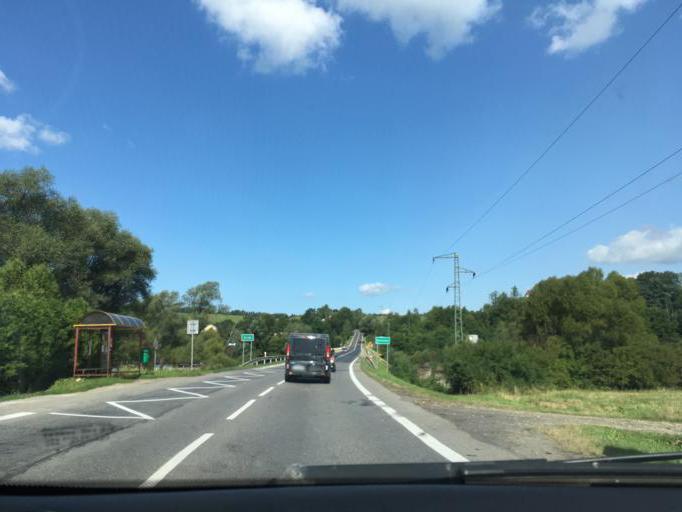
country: PL
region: Subcarpathian Voivodeship
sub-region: Powiat leski
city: Lesko
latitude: 49.4940
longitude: 22.3118
